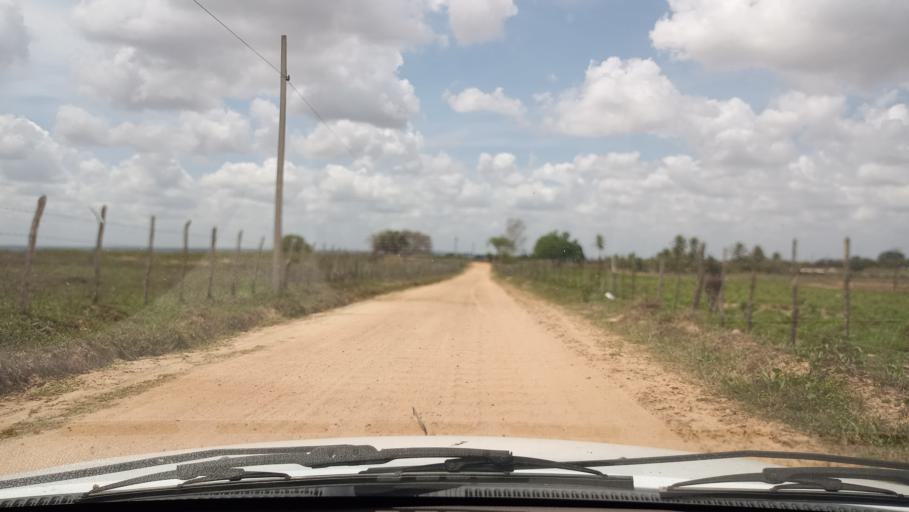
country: BR
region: Rio Grande do Norte
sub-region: Brejinho
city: Brejinho
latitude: -6.2668
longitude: -35.3435
